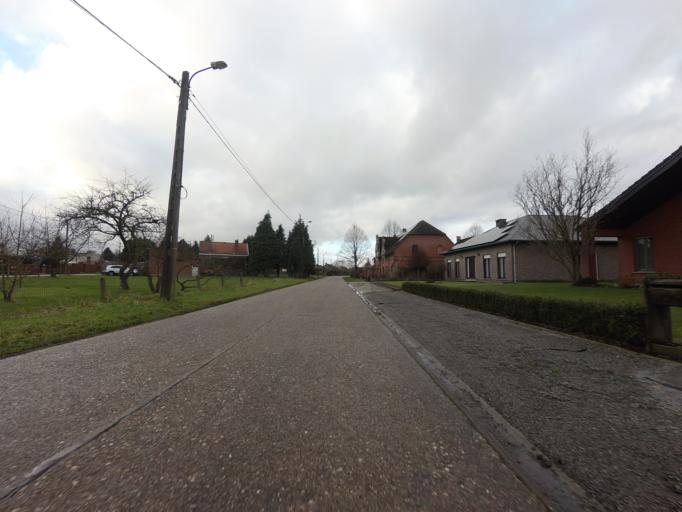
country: BE
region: Flanders
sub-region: Provincie Antwerpen
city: Lier
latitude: 51.1049
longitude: 4.5926
